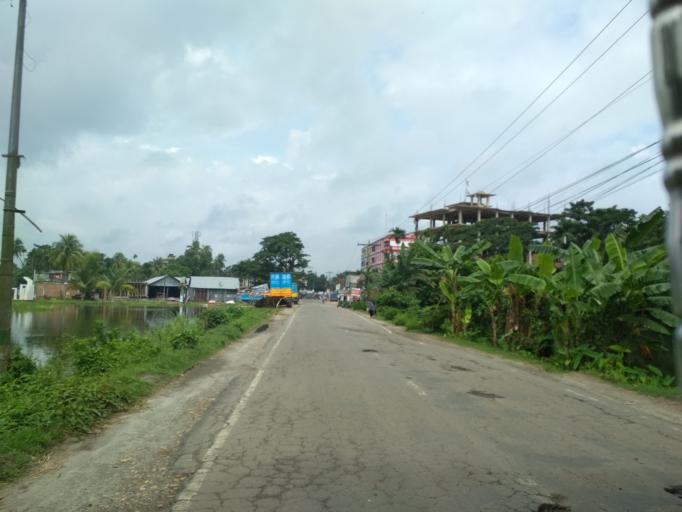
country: BD
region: Chittagong
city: Lakshmipur
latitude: 22.9684
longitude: 90.8089
